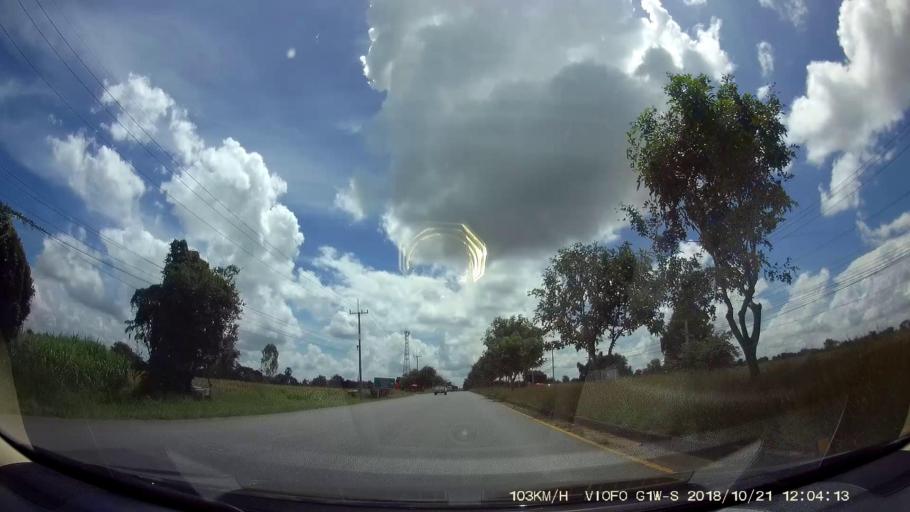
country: TH
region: Chaiyaphum
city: Chatturat
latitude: 15.4979
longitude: 101.8207
